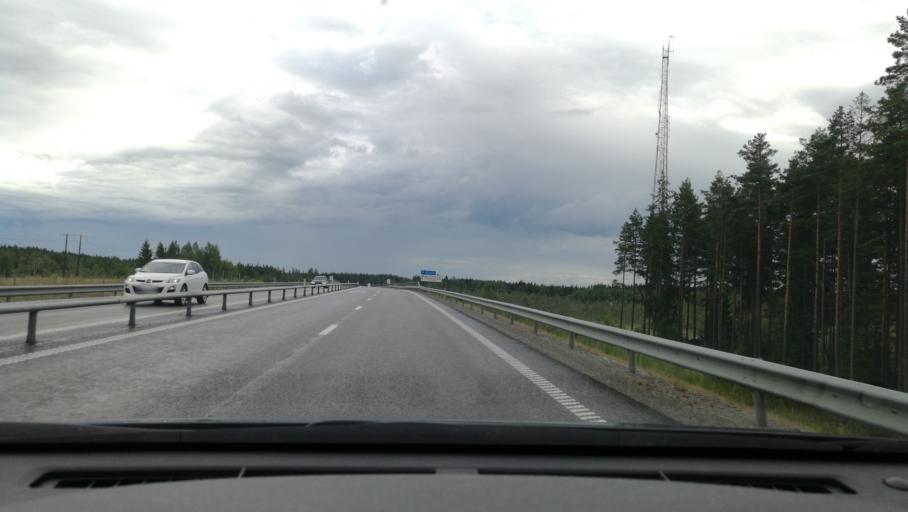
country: SE
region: Soedermanland
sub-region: Katrineholms Kommun
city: Katrineholm
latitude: 59.0016
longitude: 16.2484
